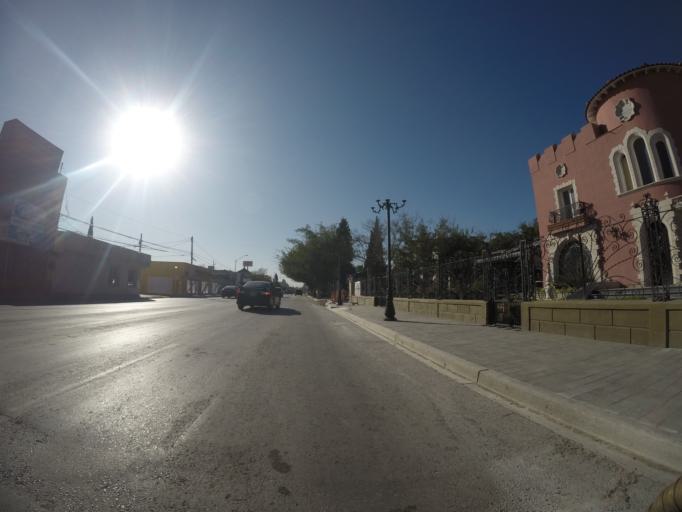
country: MX
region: Chihuahua
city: Ciudad Juarez
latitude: 31.7384
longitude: -106.4689
